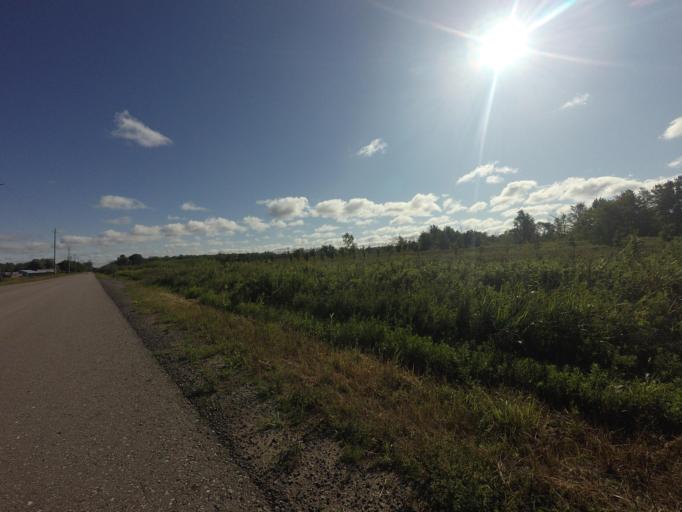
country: CA
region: Ontario
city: Bradford West Gwillimbury
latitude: 44.0506
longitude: -79.5644
